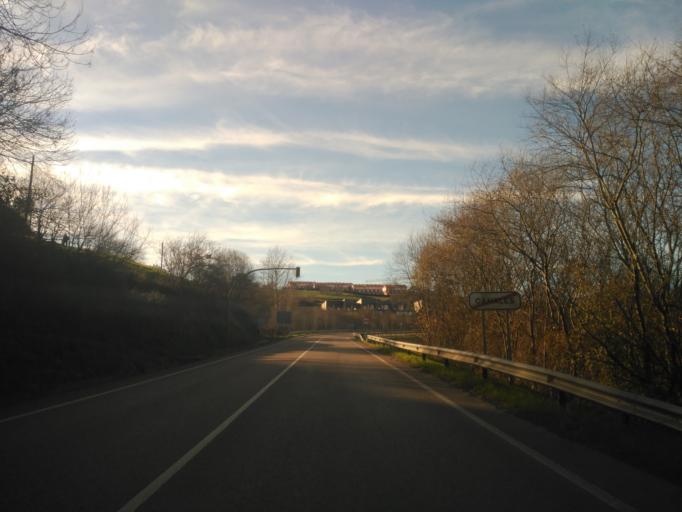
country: ES
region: Cantabria
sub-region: Provincia de Cantabria
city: Comillas
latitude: 43.3444
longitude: -4.2704
